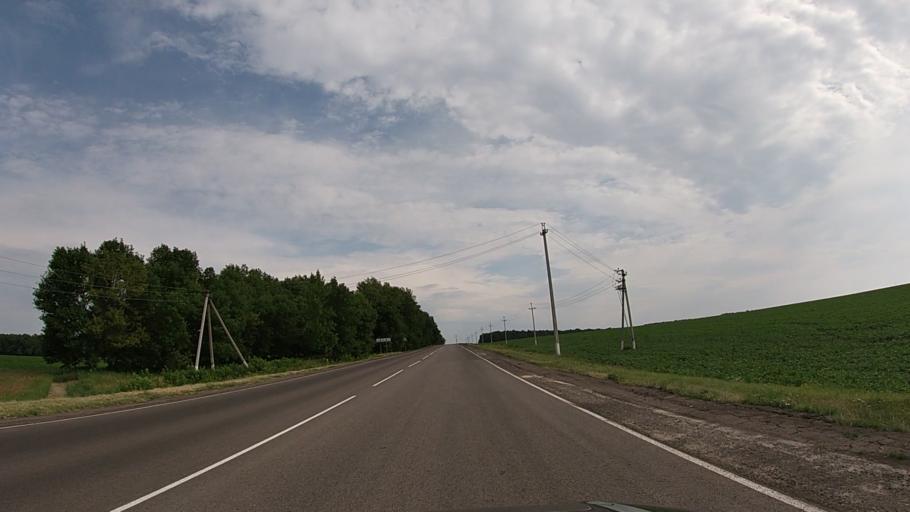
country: RU
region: Belgorod
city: Krasnaya Yaruga
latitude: 50.8097
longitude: 35.5001
